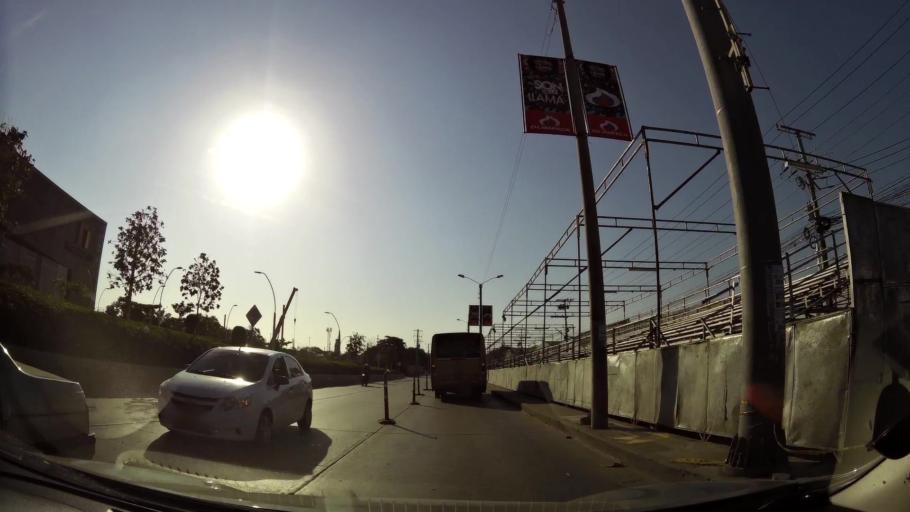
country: CO
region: Atlantico
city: Barranquilla
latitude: 11.0219
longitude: -74.7997
